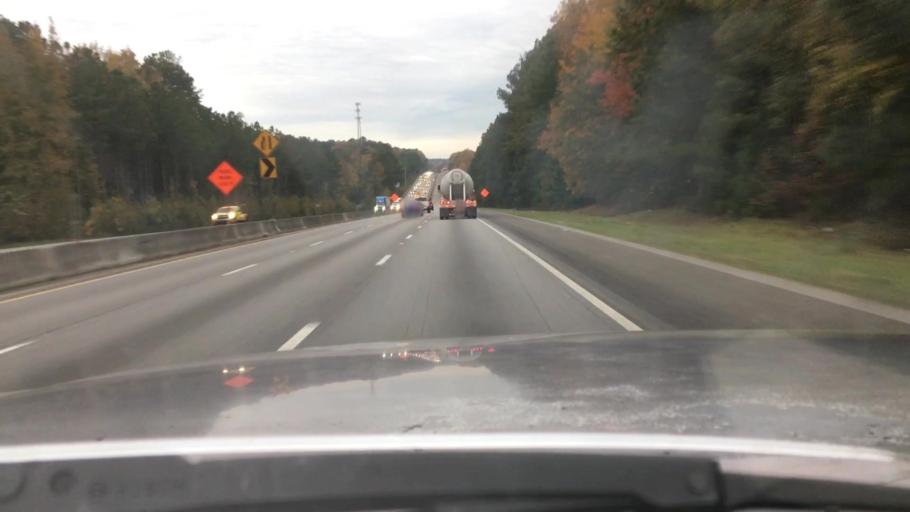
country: US
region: South Carolina
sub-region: Lexington County
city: Oak Grove
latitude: 34.0085
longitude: -81.1560
